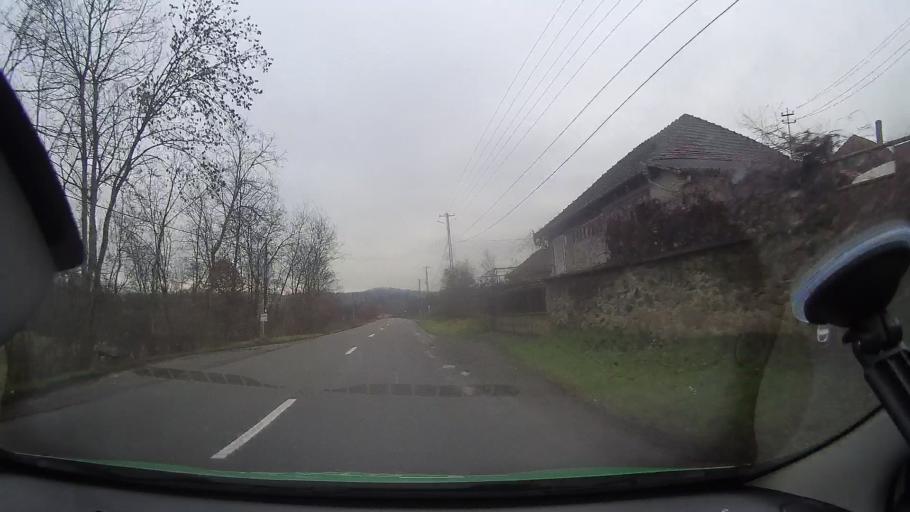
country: RO
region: Arad
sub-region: Comuna Varfurile
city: Varfurile
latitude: 46.3126
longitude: 22.5148
